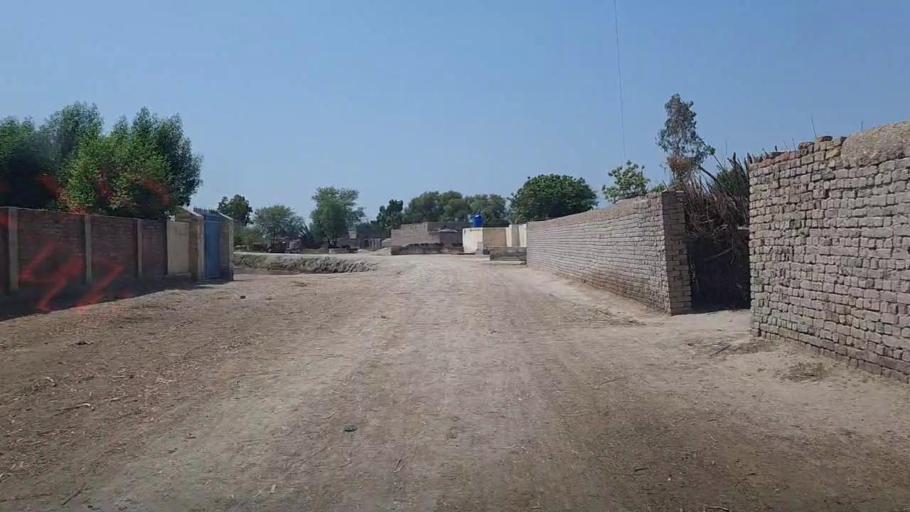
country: PK
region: Sindh
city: Ubauro
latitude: 28.1933
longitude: 69.7999
